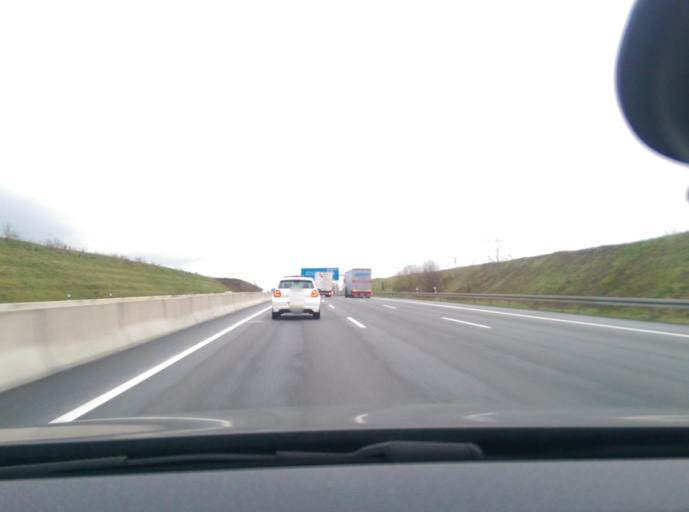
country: DE
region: Lower Saxony
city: Rosdorf
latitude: 51.5444
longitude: 9.8793
